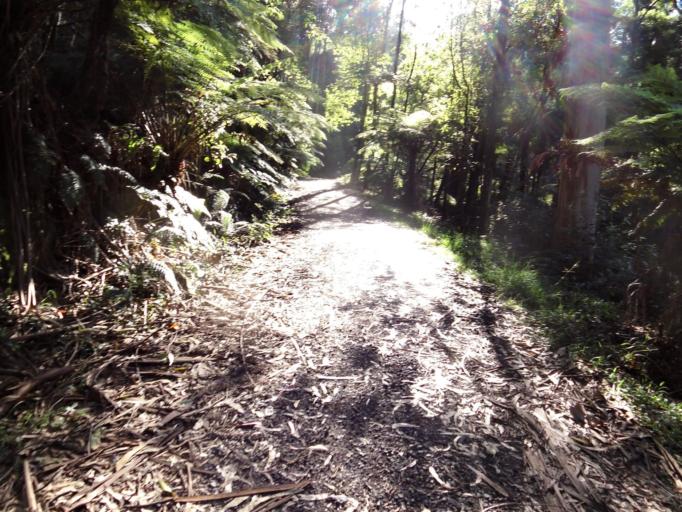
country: AU
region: Victoria
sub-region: Yarra Ranges
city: Olinda
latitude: -37.8436
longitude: 145.3475
